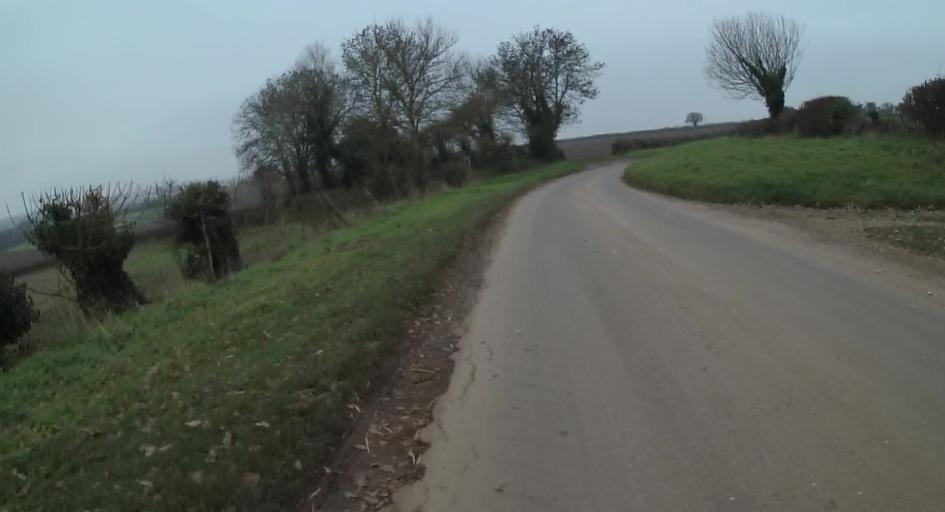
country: GB
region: England
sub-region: Hampshire
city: Kings Worthy
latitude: 51.1026
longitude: -1.2248
